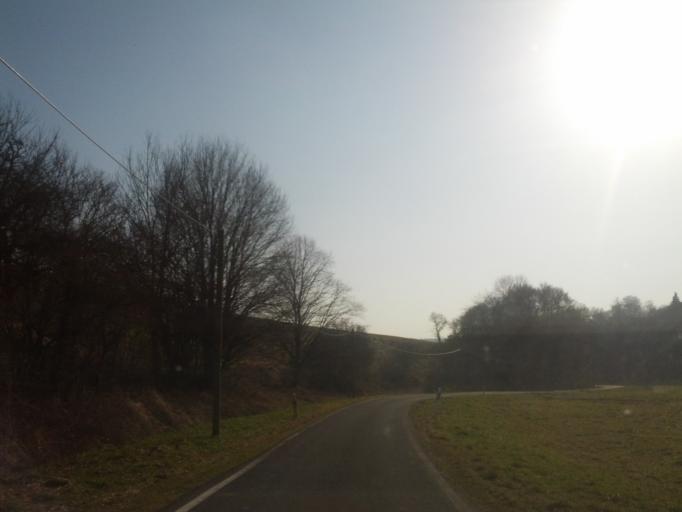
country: DE
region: Thuringia
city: Ifta
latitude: 51.0845
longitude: 10.1678
